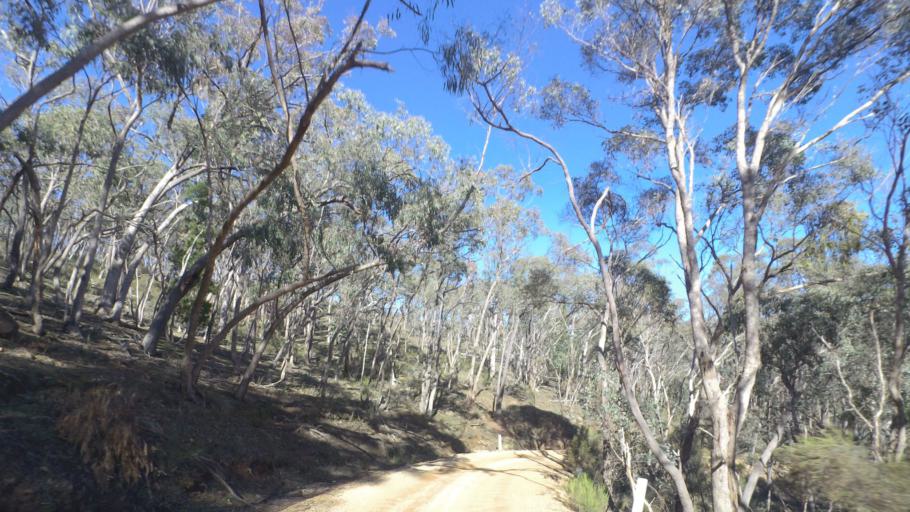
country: AU
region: Victoria
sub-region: Mount Alexander
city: Castlemaine
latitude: -37.0326
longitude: 144.2714
